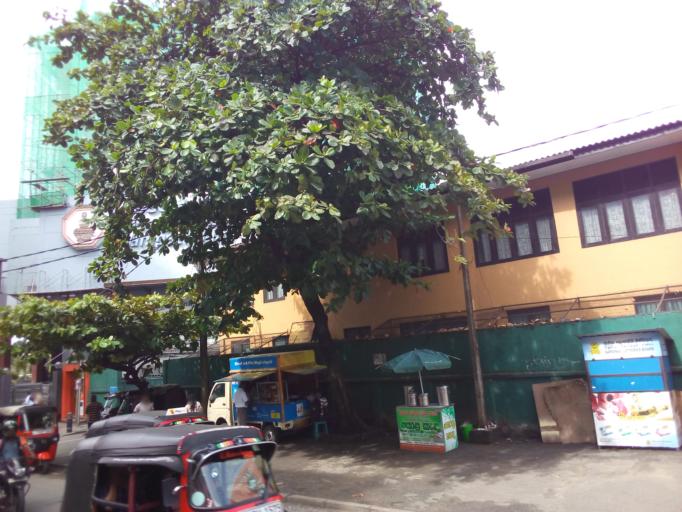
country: LK
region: Western
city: Colombo
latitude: 6.9205
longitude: 79.8533
